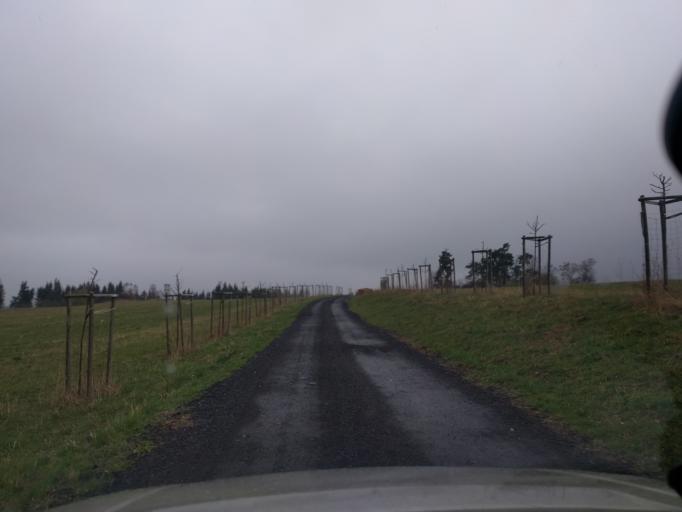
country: CZ
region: Karlovarsky
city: Bochov
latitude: 50.1126
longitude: 13.0917
